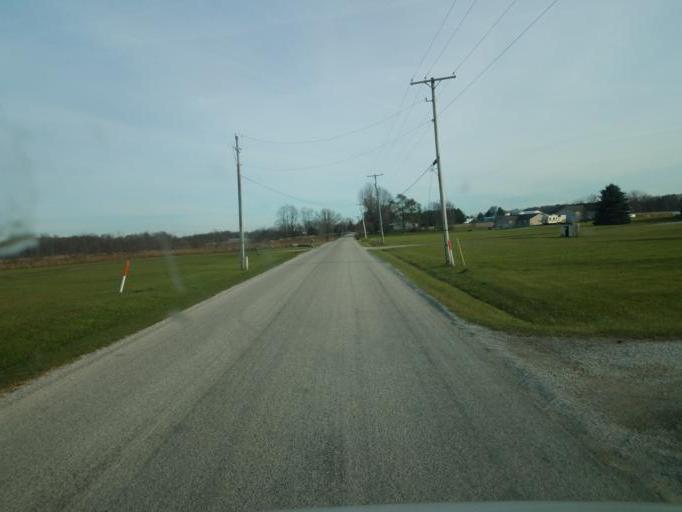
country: US
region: Ohio
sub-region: Morrow County
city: Mount Gilead
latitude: 40.5764
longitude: -82.7240
